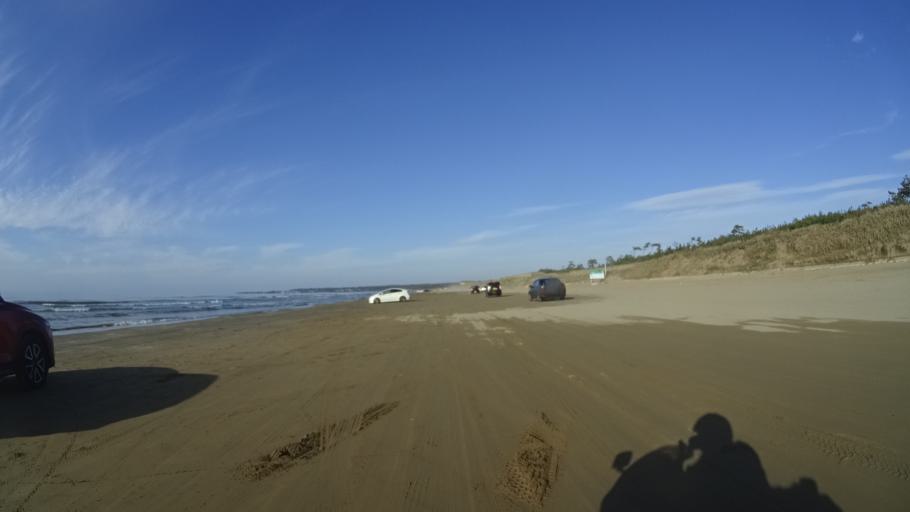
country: JP
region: Ishikawa
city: Hakui
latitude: 36.8856
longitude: 136.7635
